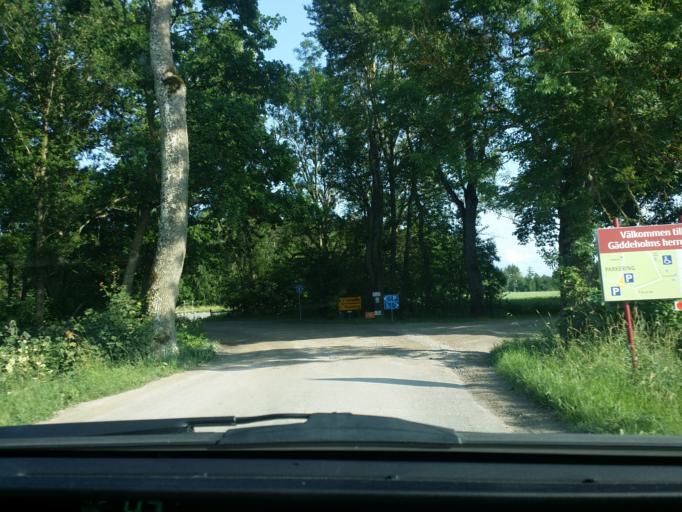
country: SE
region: Vaestmanland
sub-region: Vasteras
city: Vasteras
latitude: 59.5557
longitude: 16.6634
